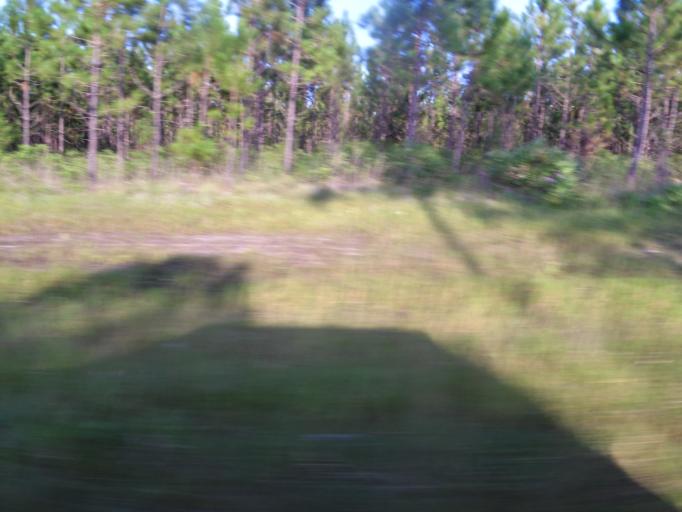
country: US
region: Florida
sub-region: Duval County
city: Baldwin
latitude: 30.3563
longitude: -82.0094
